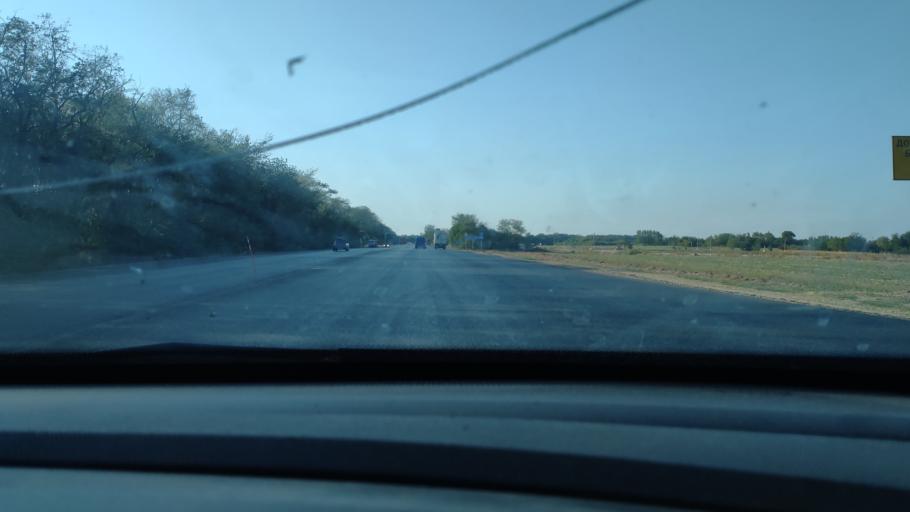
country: RU
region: Krasnodarskiy
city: Medvedovskaya
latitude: 45.4963
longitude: 38.9509
